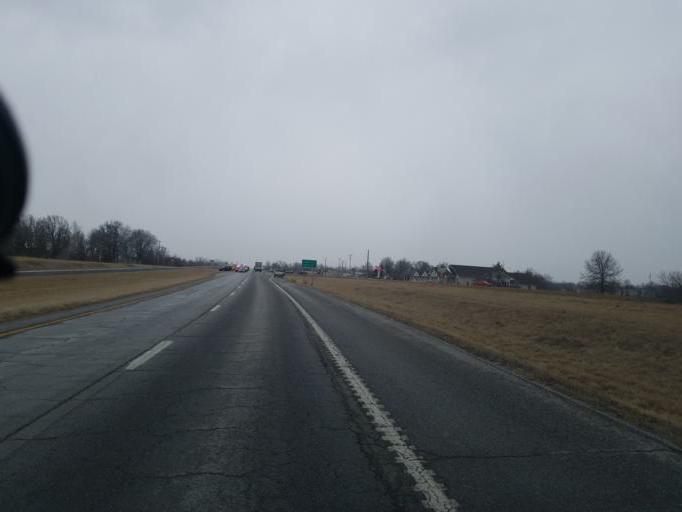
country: US
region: Missouri
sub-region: Macon County
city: La Plata
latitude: 40.0367
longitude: -92.4903
